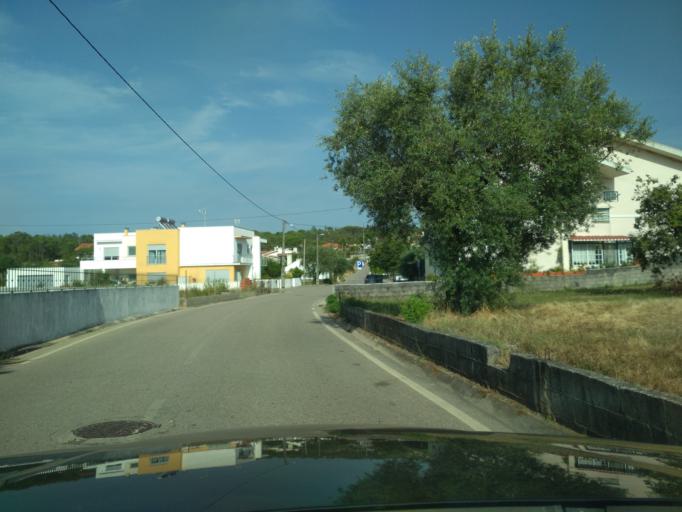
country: PT
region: Coimbra
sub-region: Condeixa-A-Nova
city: Condeixa-a-Nova
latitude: 40.1309
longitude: -8.4638
